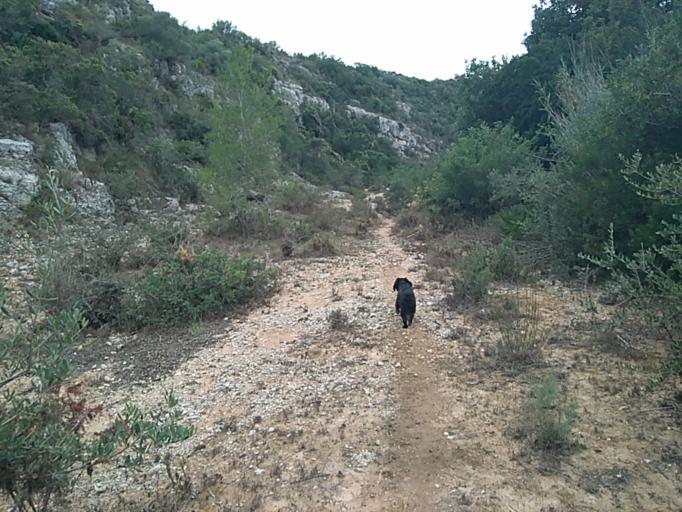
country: ES
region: Valencia
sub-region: Provincia de Valencia
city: Benimodo
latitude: 39.1919
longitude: -0.5713
